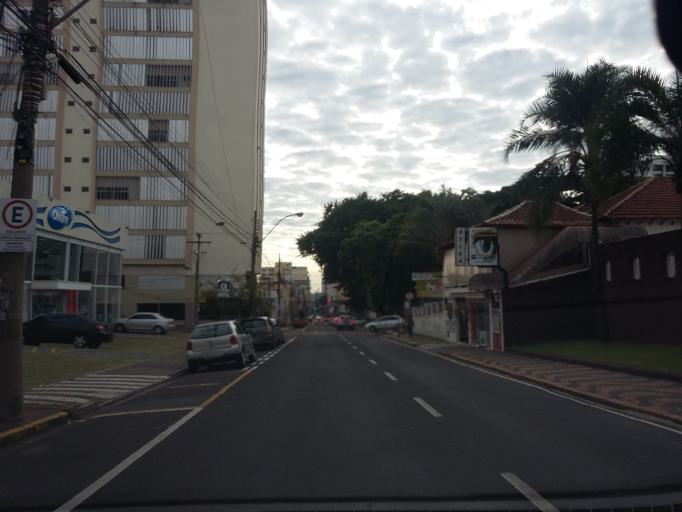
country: BR
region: Sao Paulo
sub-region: Sao Jose Do Rio Preto
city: Sao Jose do Rio Preto
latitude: -20.8164
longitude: -49.3860
